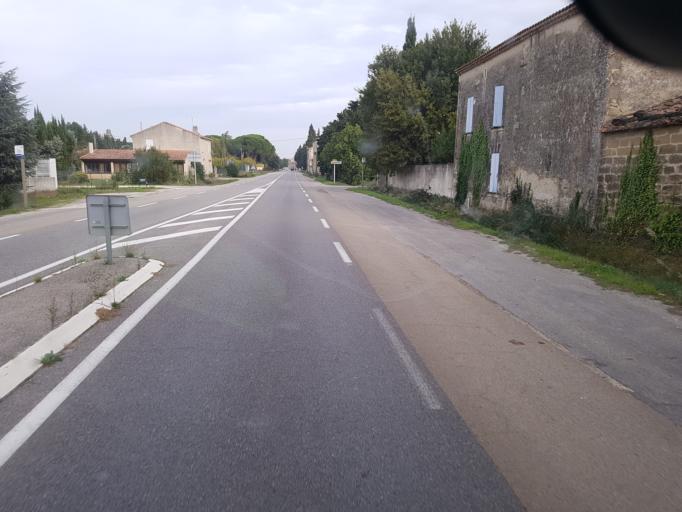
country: FR
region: Provence-Alpes-Cote d'Azur
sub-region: Departement des Bouches-du-Rhone
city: Barbentane
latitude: 43.9055
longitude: 4.7681
